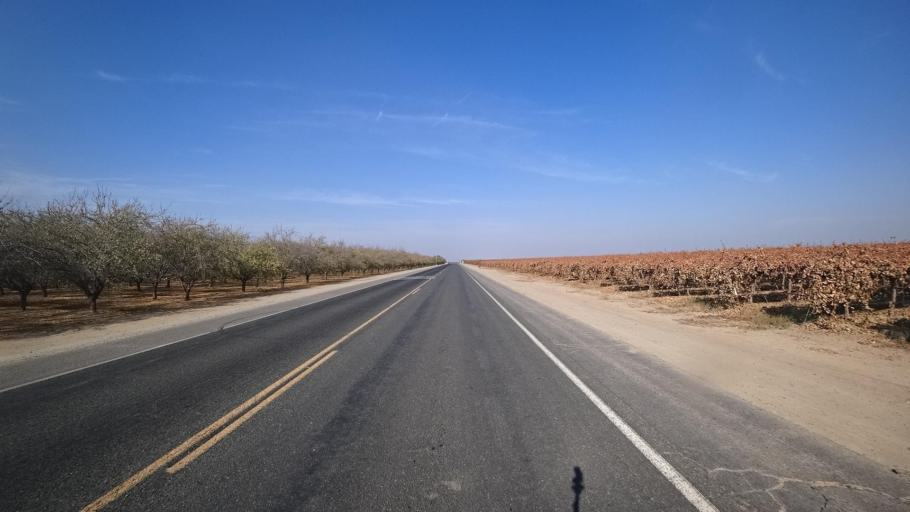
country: US
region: California
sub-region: Kern County
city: McFarland
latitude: 35.6479
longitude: -119.1956
